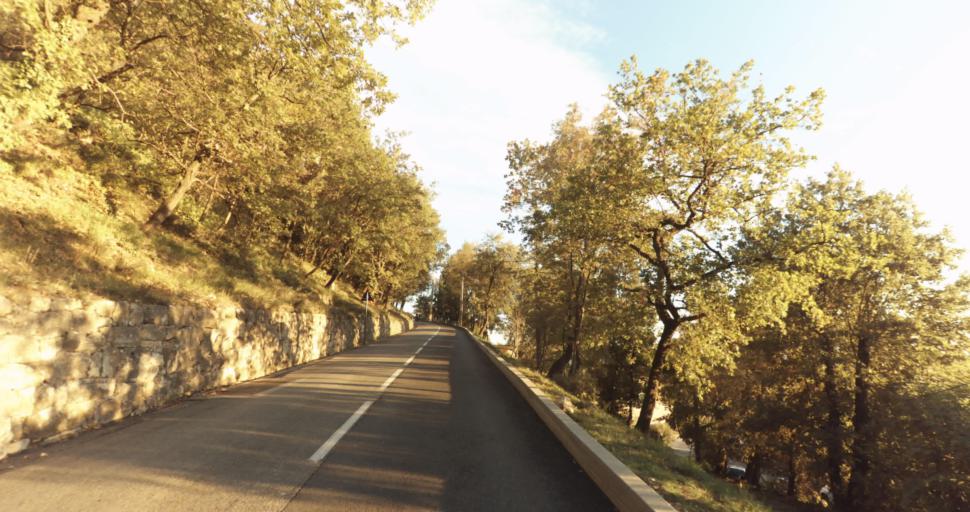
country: FR
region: Provence-Alpes-Cote d'Azur
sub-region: Departement des Alpes-Maritimes
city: Vence
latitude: 43.7306
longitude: 7.1055
